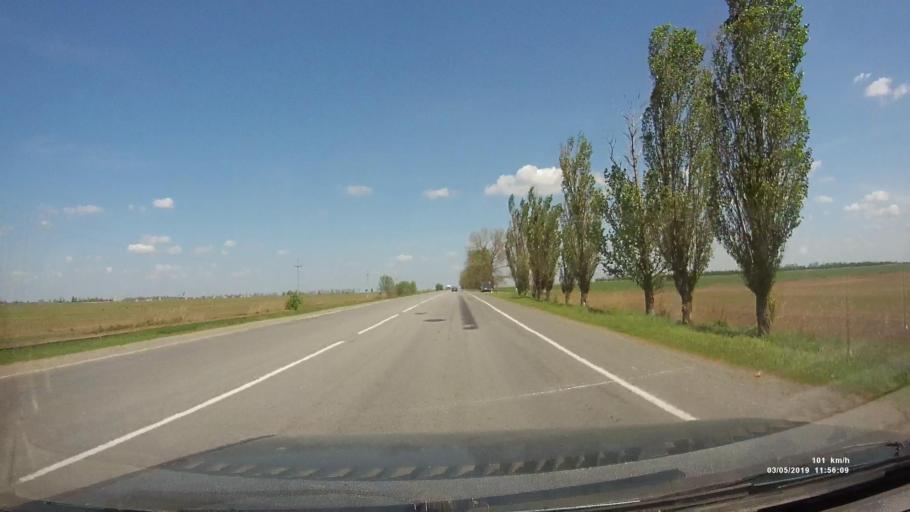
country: RU
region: Rostov
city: Bagayevskaya
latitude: 47.1907
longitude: 40.2982
